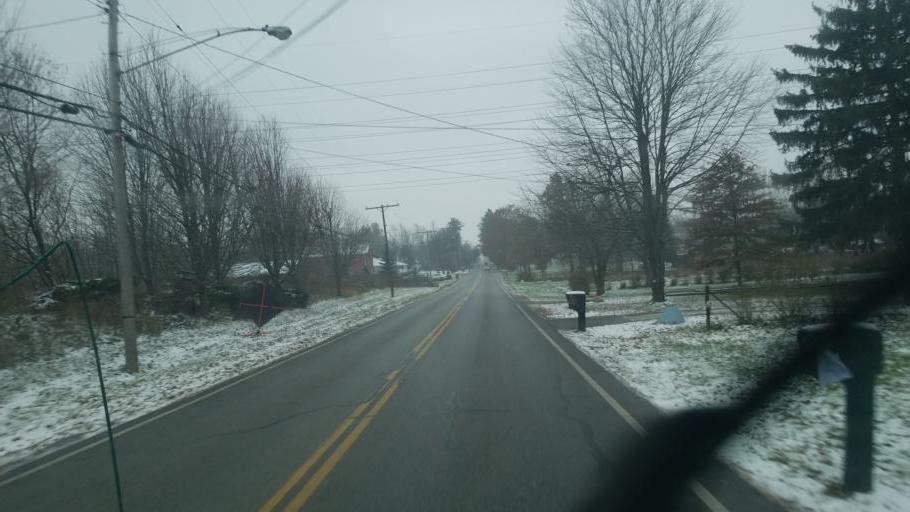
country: US
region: Ohio
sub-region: Cuyahoga County
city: Oakwood
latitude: 41.3632
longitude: -81.5082
